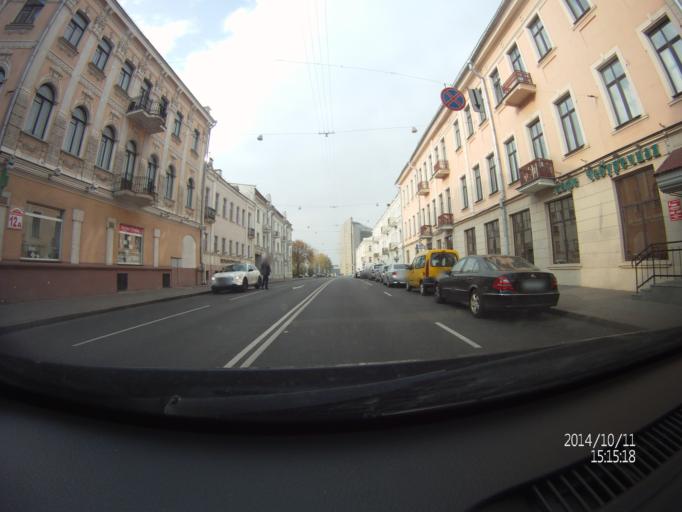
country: BY
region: Minsk
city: Minsk
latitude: 53.8974
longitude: 27.5515
